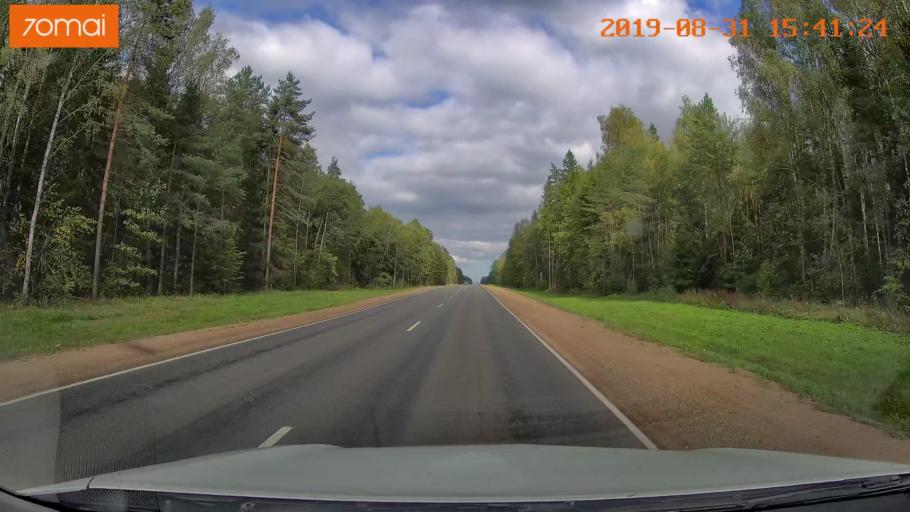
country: RU
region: Kaluga
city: Mosal'sk
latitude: 54.6389
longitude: 34.8596
